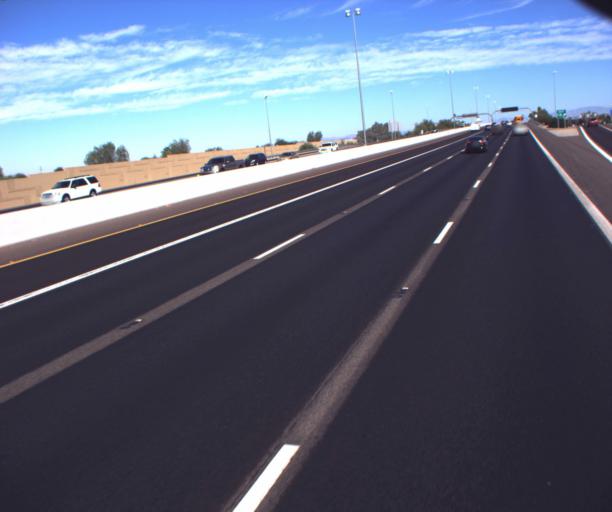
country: US
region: Arizona
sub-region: Maricopa County
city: Peoria
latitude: 33.5764
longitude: -112.2582
